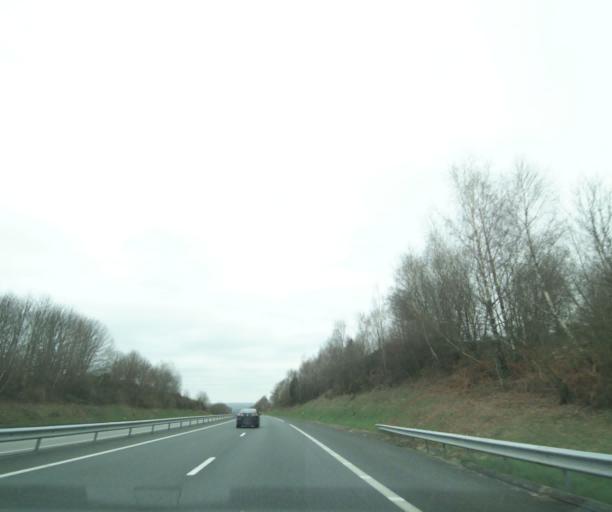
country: FR
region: Limousin
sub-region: Departement de la Correze
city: Uzerche
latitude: 45.4511
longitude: 1.5086
